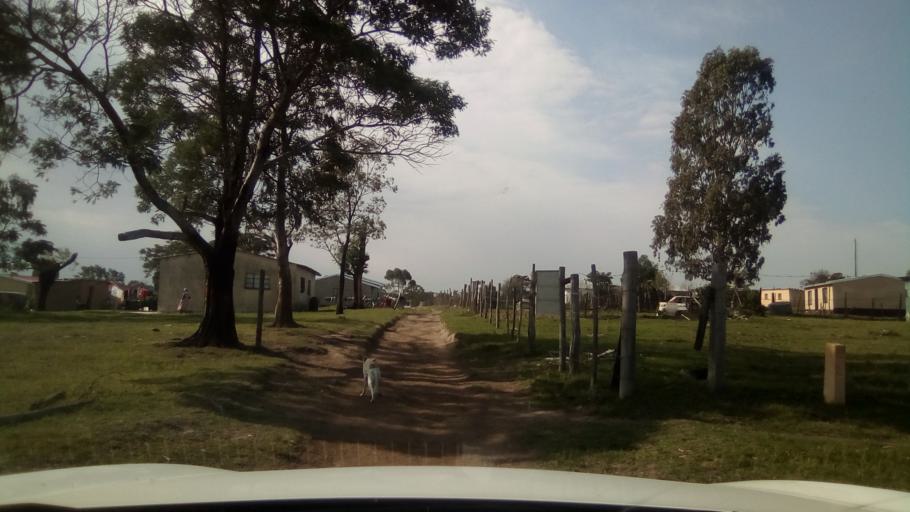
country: ZA
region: Eastern Cape
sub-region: Buffalo City Metropolitan Municipality
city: Bhisho
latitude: -32.9874
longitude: 27.2688
